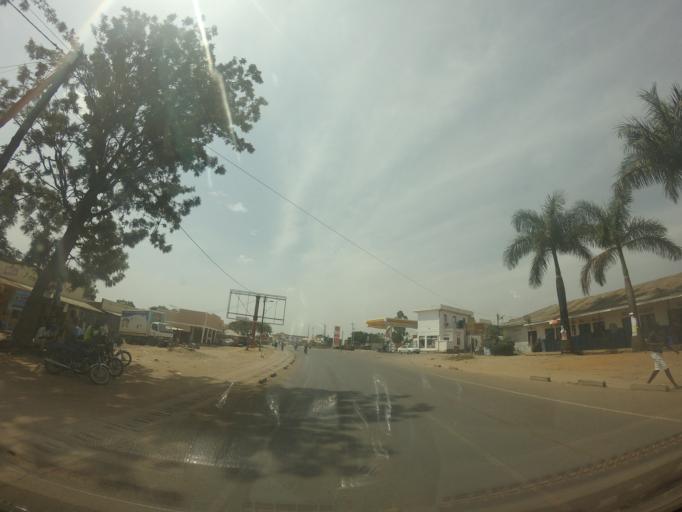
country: UG
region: Northern Region
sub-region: Arua District
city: Arua
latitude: 3.0089
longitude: 30.9114
